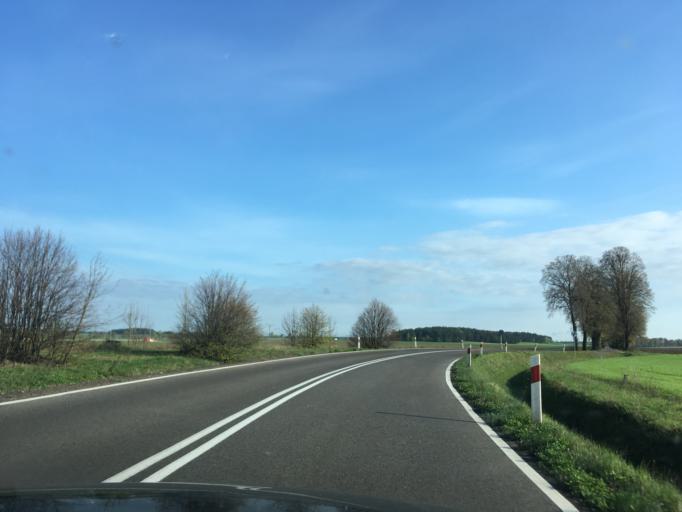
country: PL
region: Warmian-Masurian Voivodeship
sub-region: Powiat nidzicki
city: Nidzica
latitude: 53.4149
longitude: 20.3396
